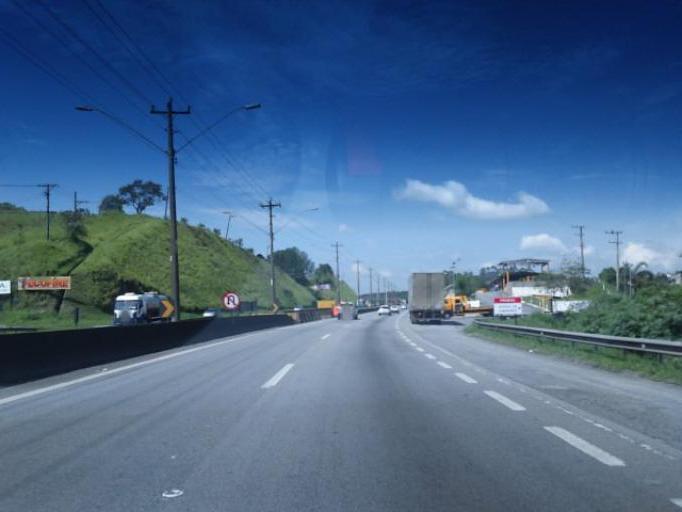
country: BR
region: Sao Paulo
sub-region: Itapecerica Da Serra
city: Itapecerica da Serra
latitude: -23.6995
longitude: -46.8675
